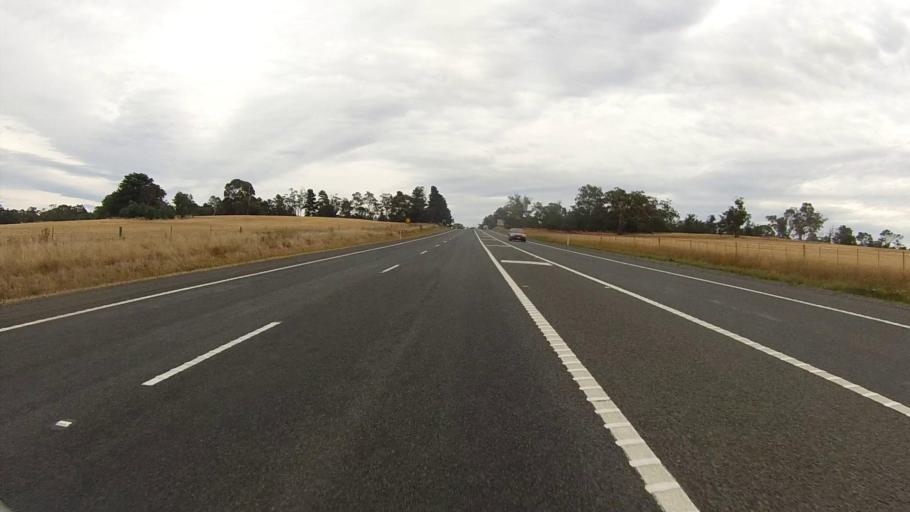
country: AU
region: Tasmania
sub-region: Northern Midlands
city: Evandale
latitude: -41.8339
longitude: 147.4458
